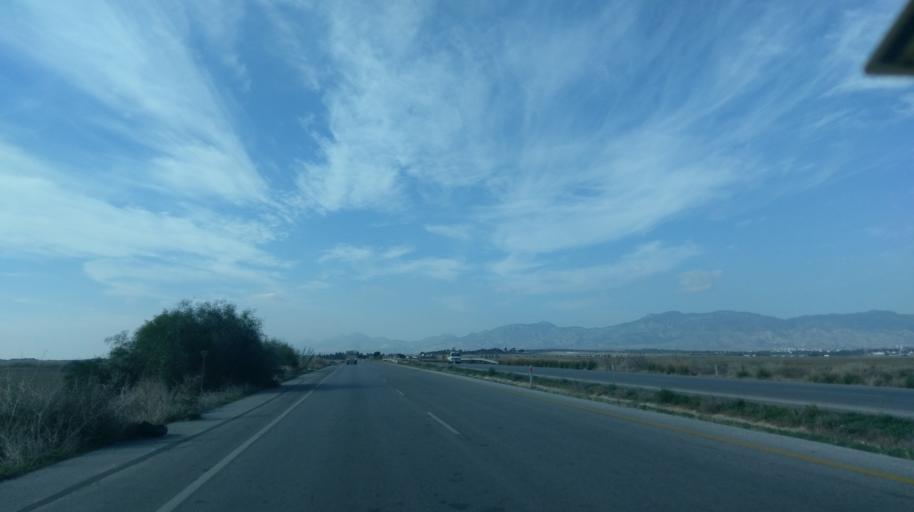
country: CY
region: Ammochostos
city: Lefkonoiko
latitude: 35.1885
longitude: 33.6311
